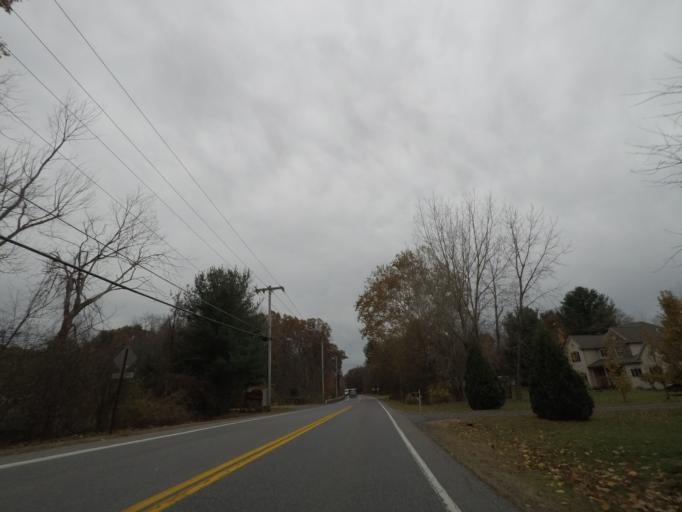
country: US
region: New York
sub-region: Schenectady County
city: Niskayuna
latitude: 42.8420
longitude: -73.8203
